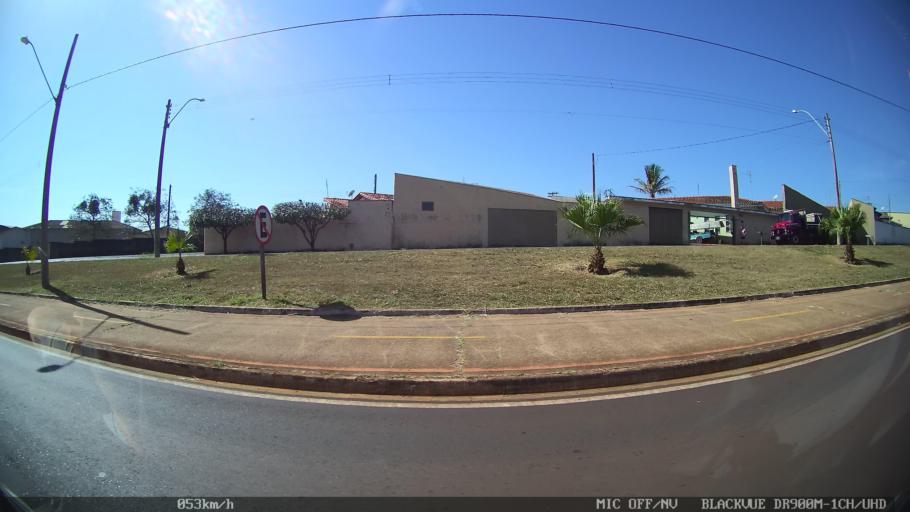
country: BR
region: Sao Paulo
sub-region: Batatais
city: Batatais
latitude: -20.9127
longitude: -47.5831
